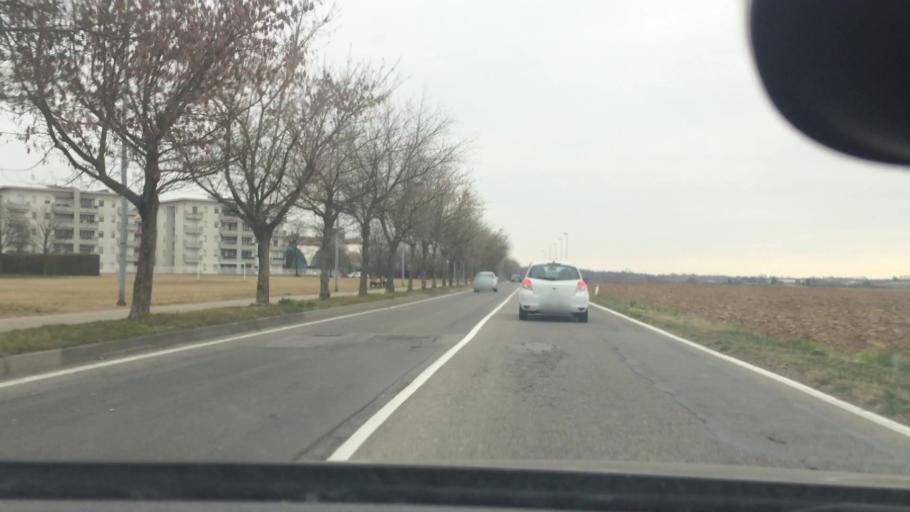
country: IT
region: Lombardy
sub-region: Citta metropolitana di Milano
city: Solaro
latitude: 45.6142
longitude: 9.0717
